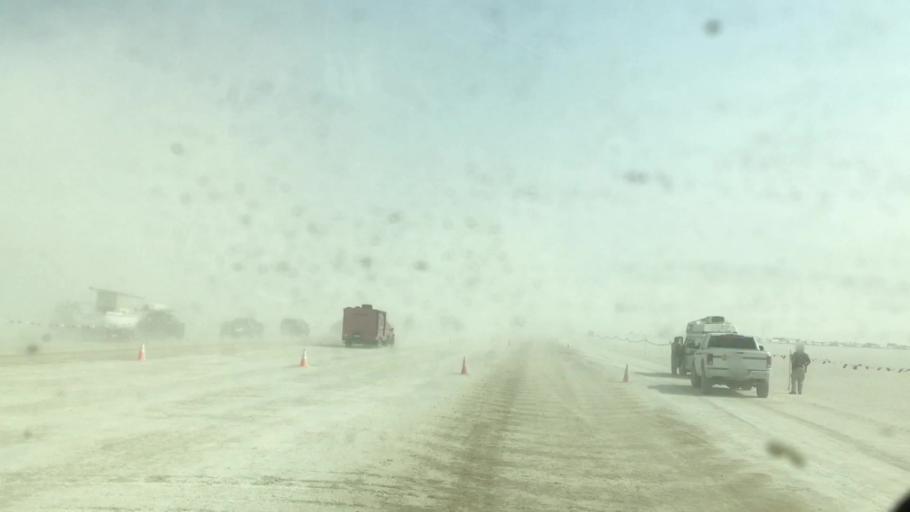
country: US
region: Nevada
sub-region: Pershing County
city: Lovelock
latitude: 40.7635
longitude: -119.2499
